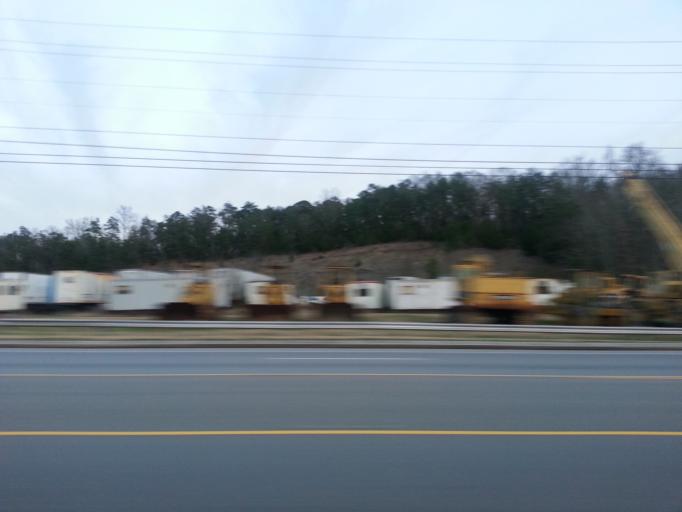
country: US
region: Tennessee
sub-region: McMinn County
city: Etowah
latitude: 35.3541
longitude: -84.5209
